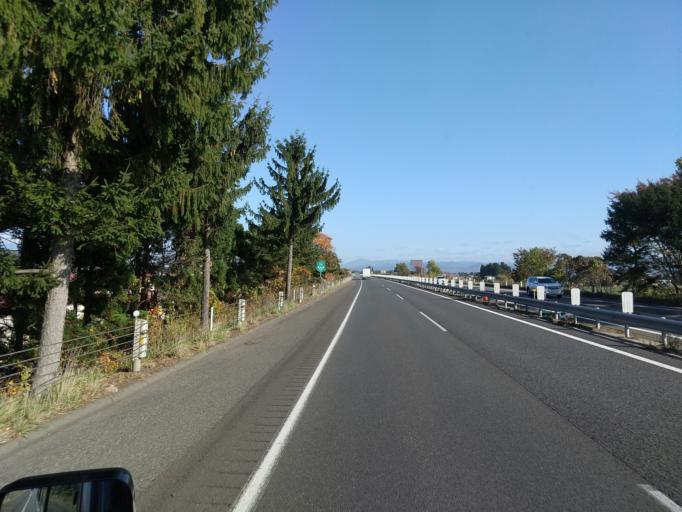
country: JP
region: Iwate
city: Morioka-shi
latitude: 39.5593
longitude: 141.1170
